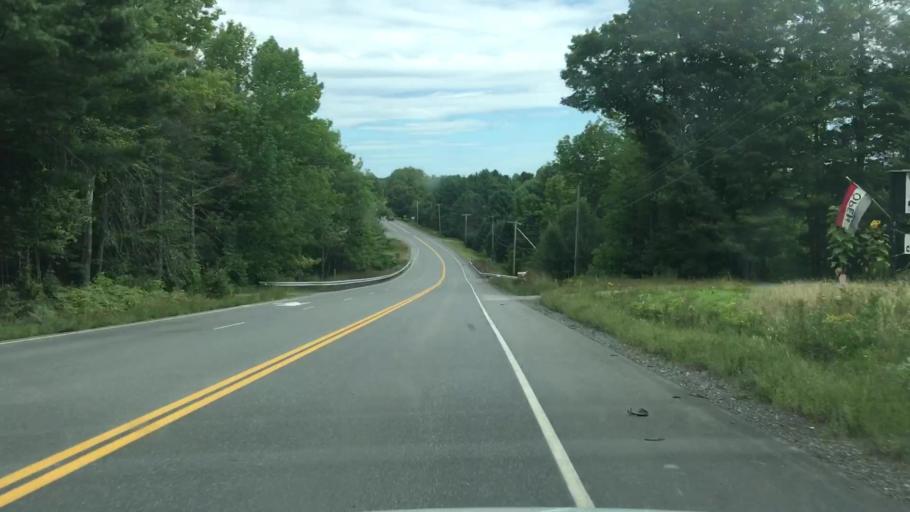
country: US
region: Maine
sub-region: Piscataquis County
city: Milo
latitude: 45.2371
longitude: -69.0529
